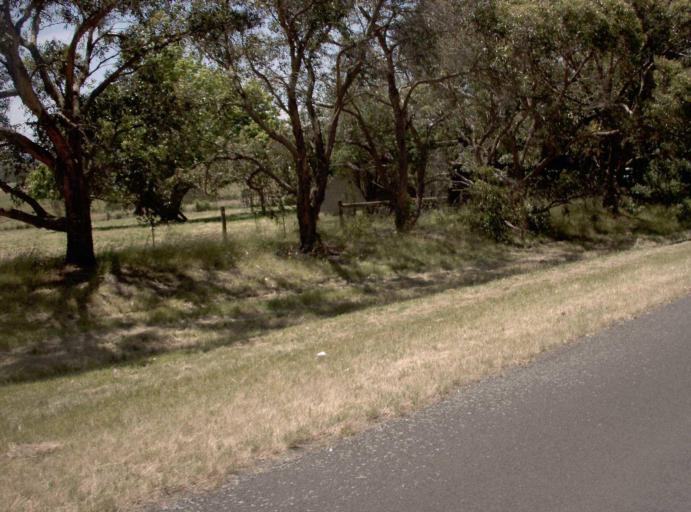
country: AU
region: Victoria
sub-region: Cardinia
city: Bunyip
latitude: -38.0787
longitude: 145.7437
